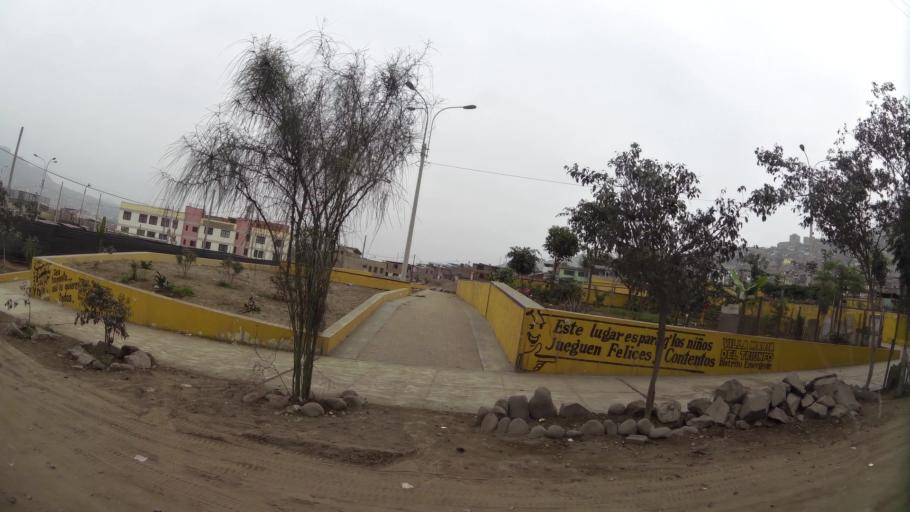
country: PE
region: Lima
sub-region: Lima
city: Surco
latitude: -12.1757
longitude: -76.9499
